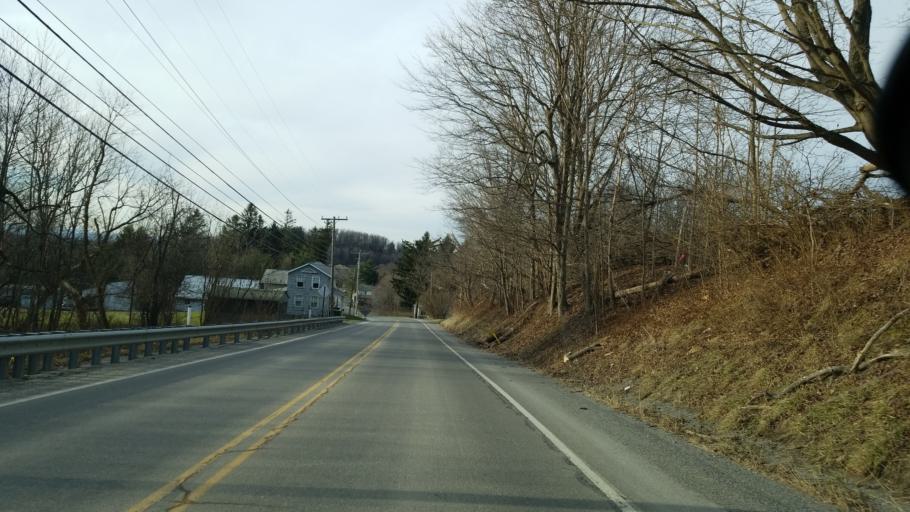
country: US
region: Pennsylvania
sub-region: Clearfield County
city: Sandy
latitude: 41.0495
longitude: -78.7044
